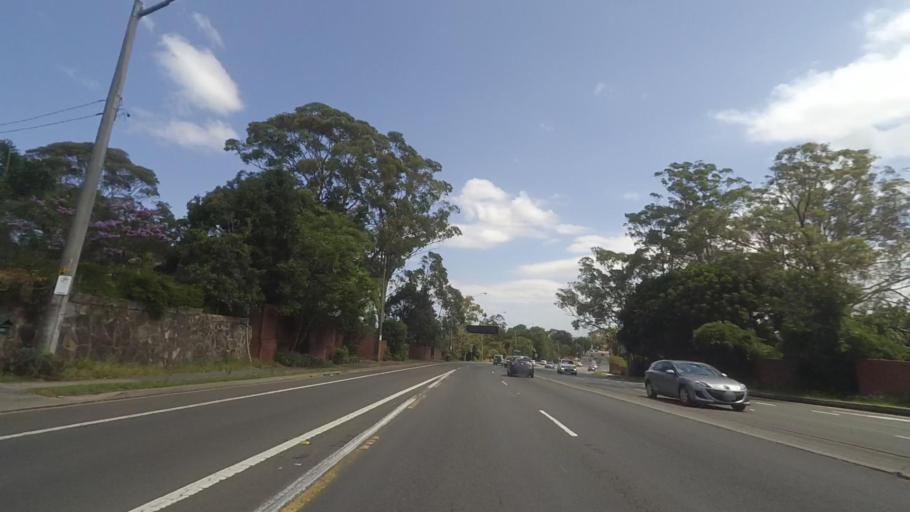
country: AU
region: New South Wales
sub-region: The Hills Shire
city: West Pennant
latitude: -33.7506
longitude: 151.0492
